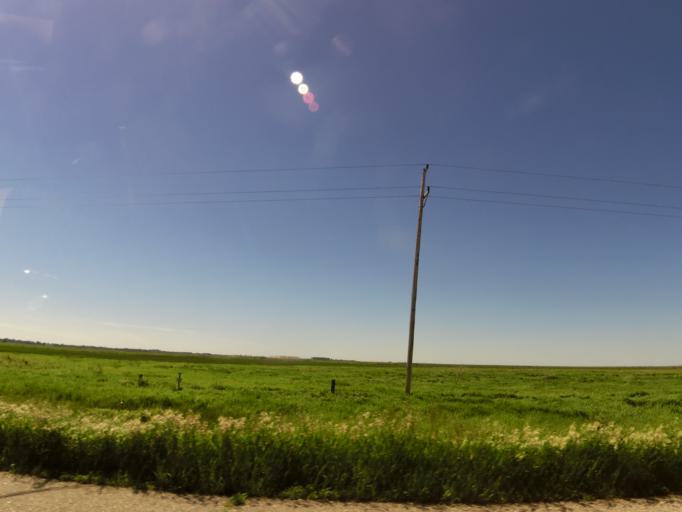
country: US
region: Minnesota
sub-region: Red Lake County
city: Red Lake Falls
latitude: 47.7601
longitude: -96.3049
